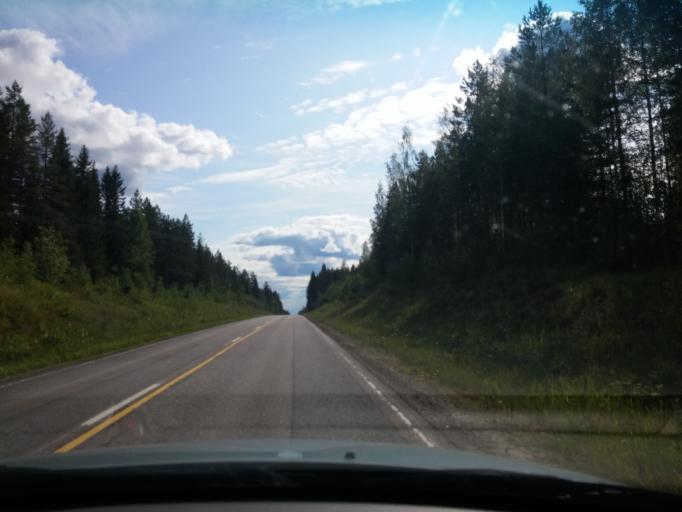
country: FI
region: Central Finland
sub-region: Keuruu
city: Keuruu
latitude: 62.3071
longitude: 24.7276
